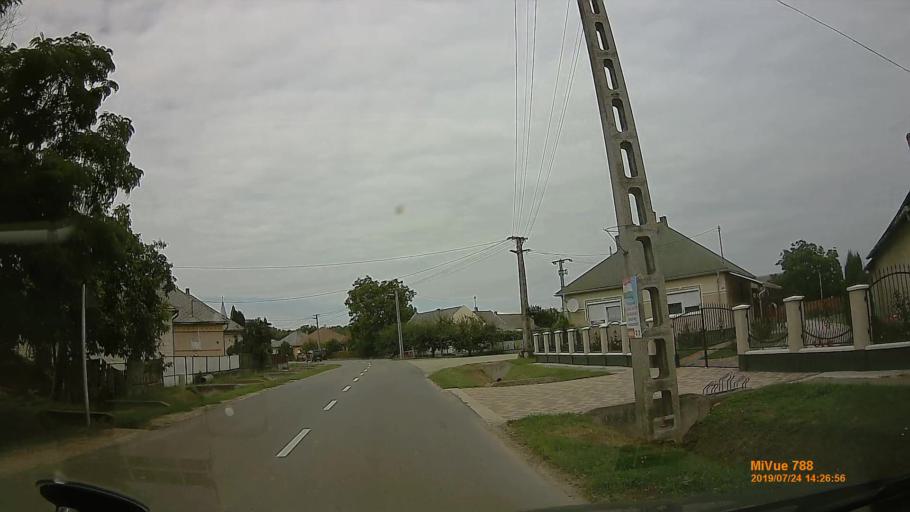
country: HU
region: Szabolcs-Szatmar-Bereg
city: Mandok
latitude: 48.3298
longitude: 22.2654
